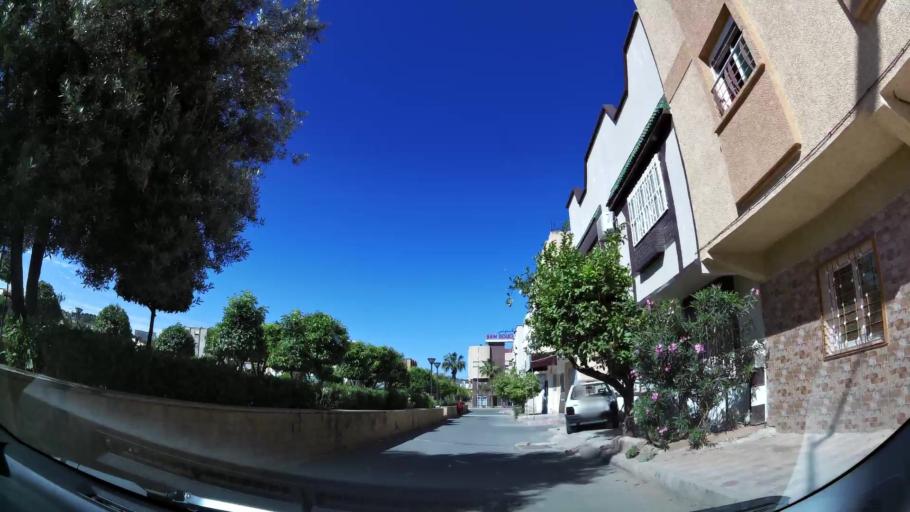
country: MA
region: Oriental
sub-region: Oujda-Angad
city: Oujda
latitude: 34.6546
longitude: -1.8954
